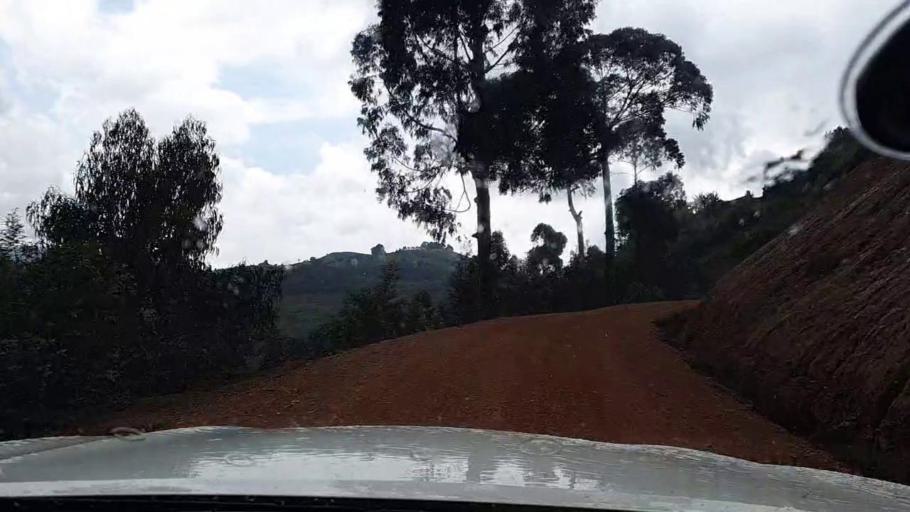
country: RW
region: Western Province
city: Kibuye
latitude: -2.1494
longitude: 29.4263
